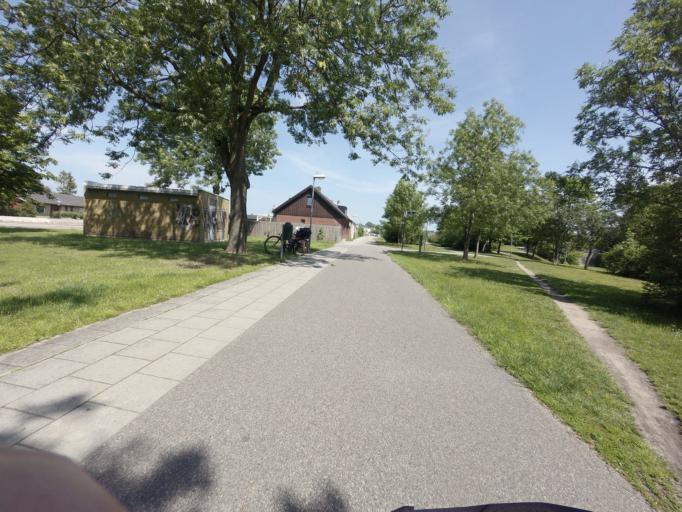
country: SE
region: Skane
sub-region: Malmo
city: Bunkeflostrand
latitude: 55.5757
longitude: 12.9248
